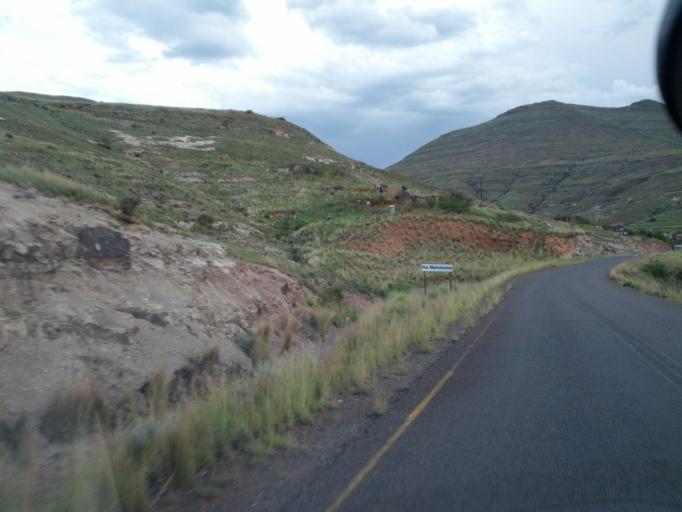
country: LS
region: Qacha's Nek
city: Qacha's Nek
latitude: -30.0736
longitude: 28.5821
